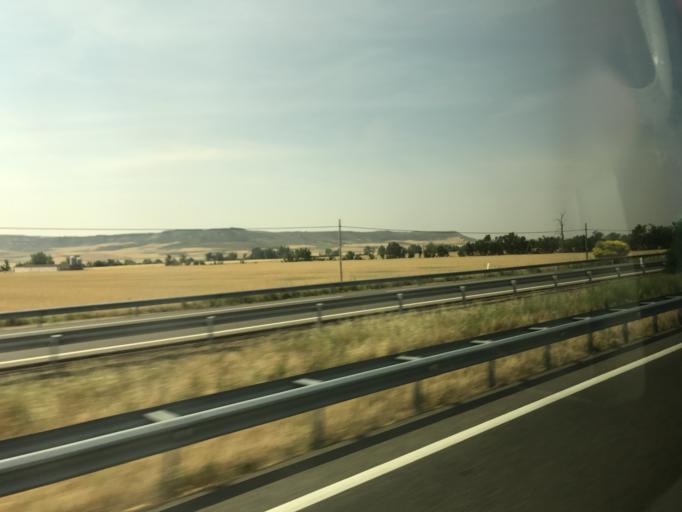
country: ES
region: Castille and Leon
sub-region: Provincia de Palencia
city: Villodrigo
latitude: 42.1354
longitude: -4.1162
